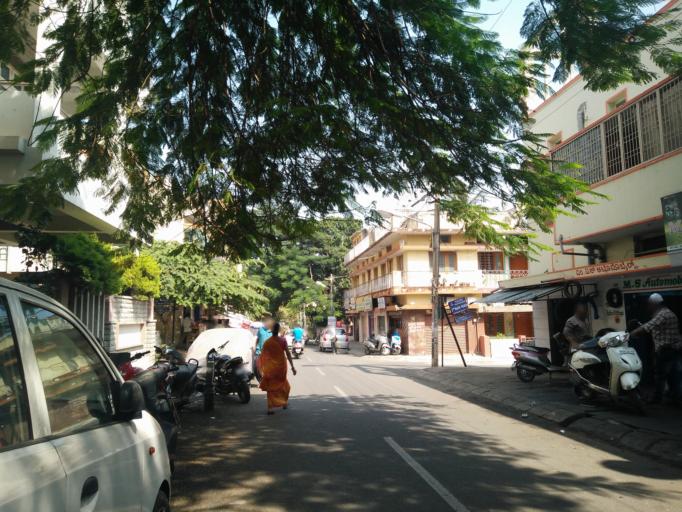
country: IN
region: Karnataka
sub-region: Bangalore Urban
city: Bangalore
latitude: 12.9722
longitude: 77.5454
